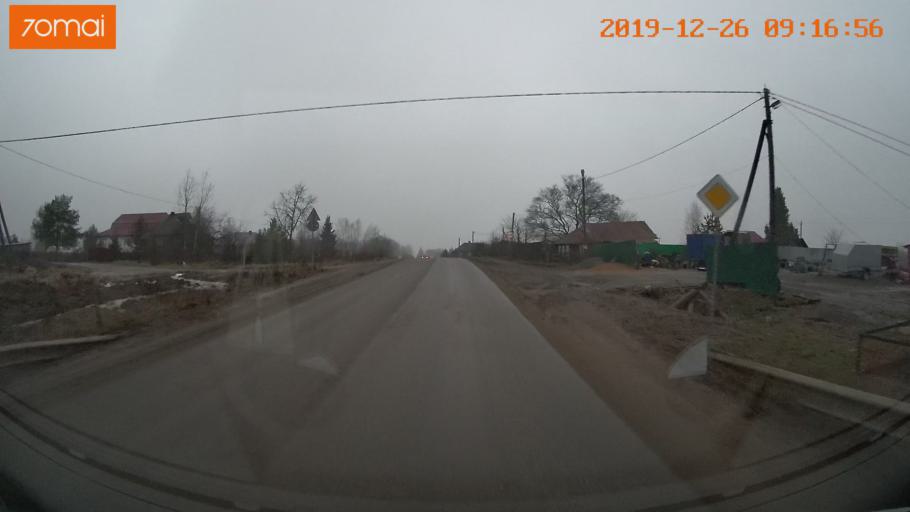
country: RU
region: Vologda
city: Gryazovets
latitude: 58.9243
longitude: 40.2392
